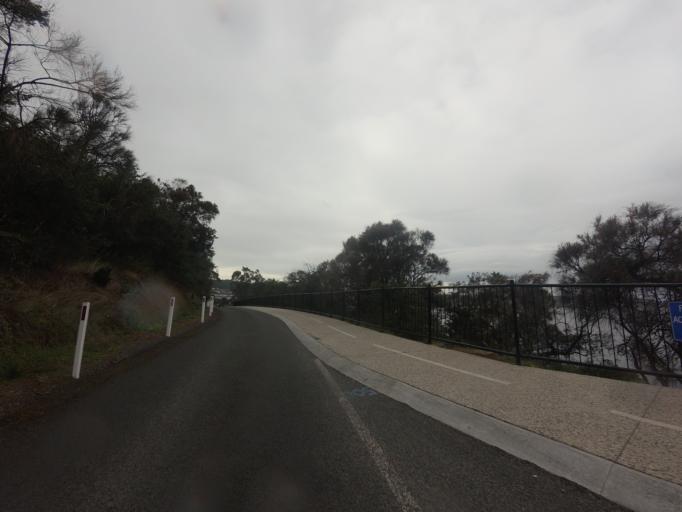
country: AU
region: Tasmania
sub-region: Clarence
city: Bellerive
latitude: -42.8823
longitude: 147.3677
